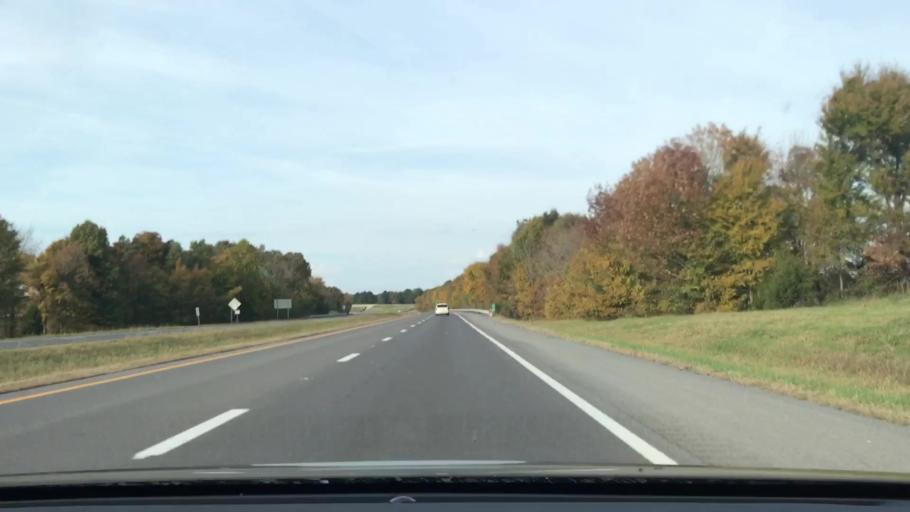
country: US
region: Kentucky
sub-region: Graves County
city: Mayfield
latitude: 36.7777
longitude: -88.5854
